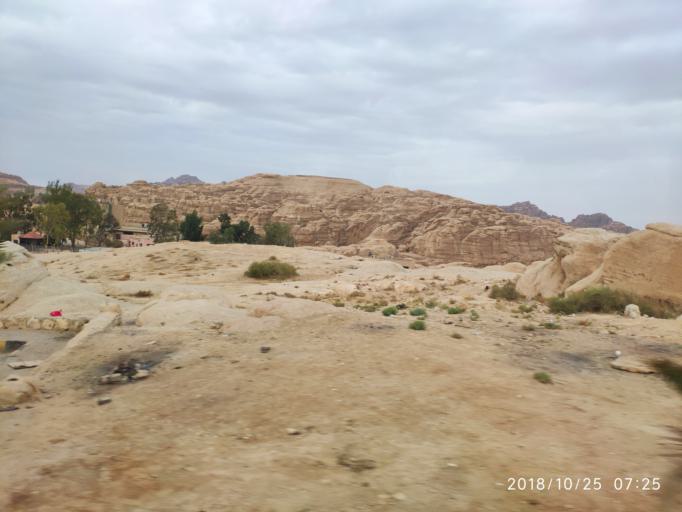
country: JO
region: Ma'an
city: Petra
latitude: 30.3272
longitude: 35.4680
